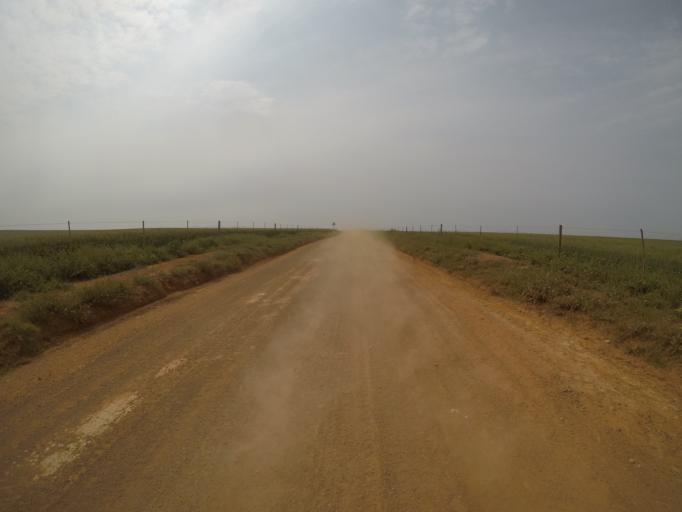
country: ZA
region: Western Cape
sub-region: City of Cape Town
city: Kraaifontein
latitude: -33.7223
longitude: 18.6729
